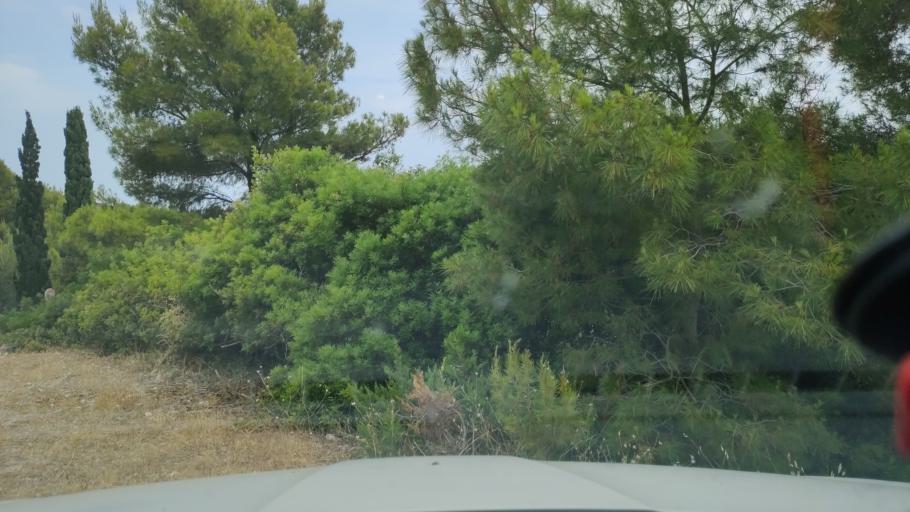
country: HR
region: Splitsko-Dalmatinska
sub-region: Grad Vis
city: Vis
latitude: 43.0245
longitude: 16.1693
